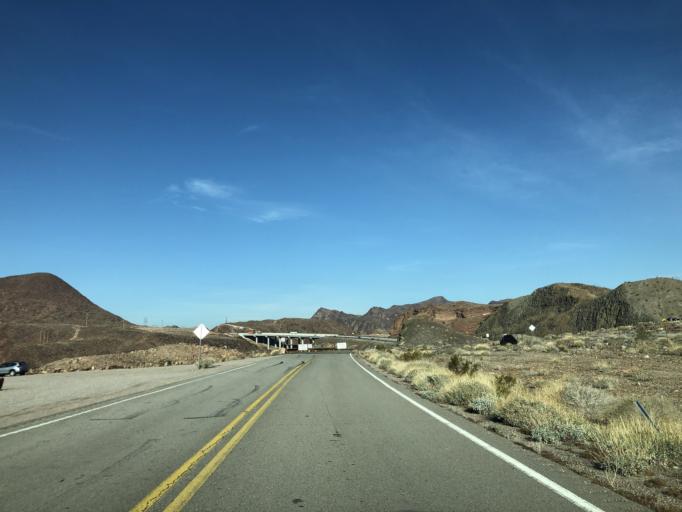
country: US
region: Nevada
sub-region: Clark County
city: Boulder City
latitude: 36.0024
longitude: -114.7236
